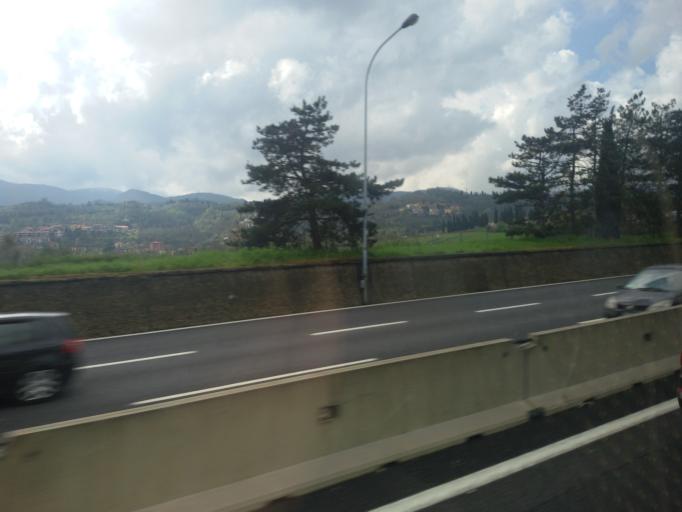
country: IT
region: Tuscany
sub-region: Province of Florence
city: Incisa in Val d'Arno
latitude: 43.6621
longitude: 11.4612
